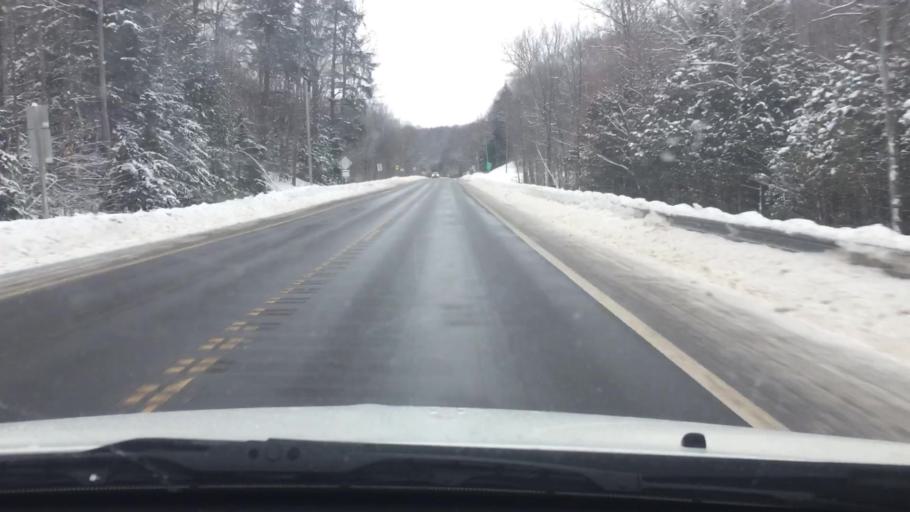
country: US
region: Michigan
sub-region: Charlevoix County
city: East Jordan
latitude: 45.1169
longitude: -85.0607
